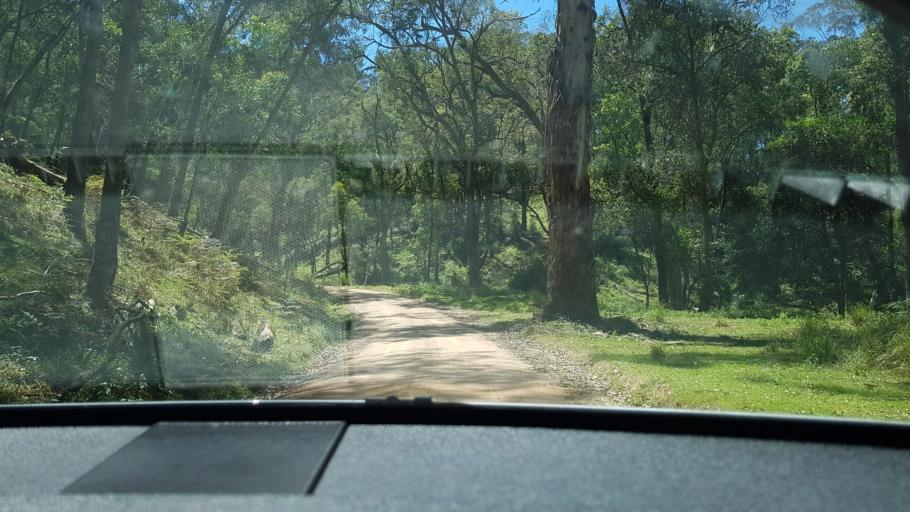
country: AU
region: New South Wales
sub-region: Blue Mountains Municipality
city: Katoomba
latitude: -33.7753
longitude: 150.2345
